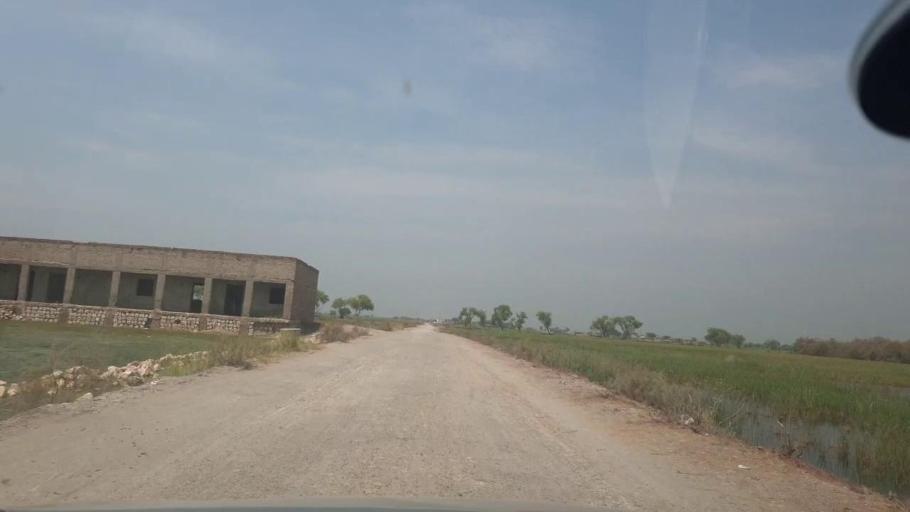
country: PK
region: Sindh
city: Thul
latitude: 28.1690
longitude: 68.6346
